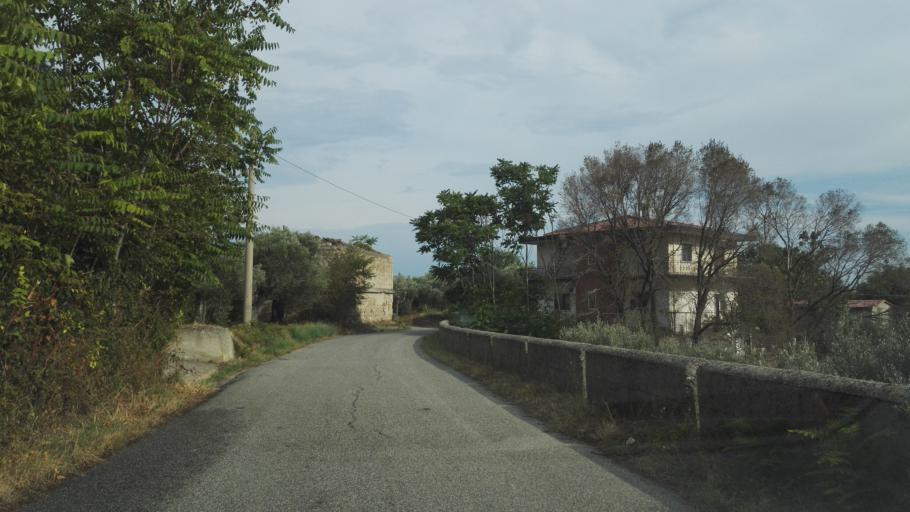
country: IT
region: Calabria
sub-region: Provincia di Reggio Calabria
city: Stignano
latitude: 38.4260
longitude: 16.4645
